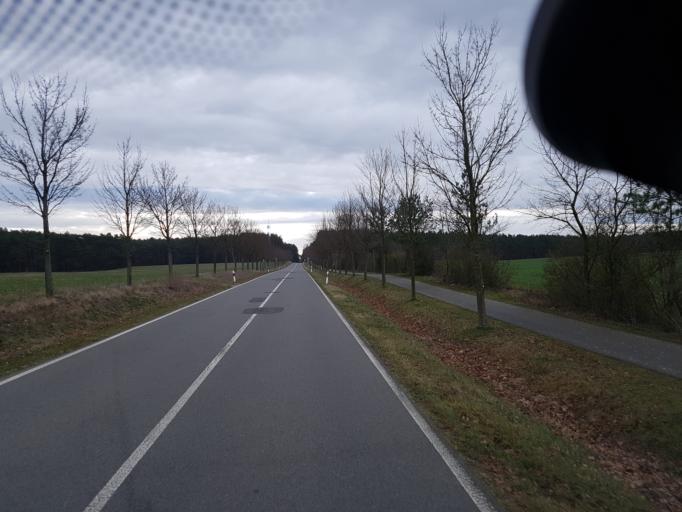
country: DE
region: Brandenburg
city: Mixdorf
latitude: 52.1938
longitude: 14.4137
